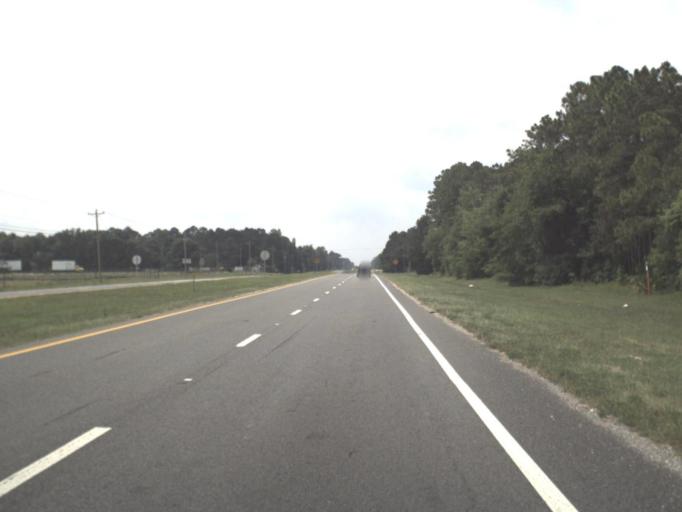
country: US
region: Florida
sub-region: Clay County
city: Green Cove Springs
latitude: 29.8715
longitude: -81.6640
